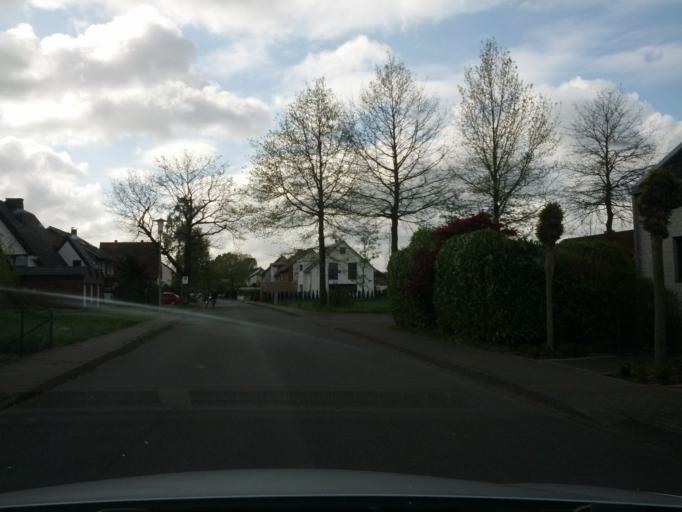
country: DE
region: North Rhine-Westphalia
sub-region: Regierungsbezirk Detmold
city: Guetersloh
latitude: 51.8819
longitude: 8.3854
